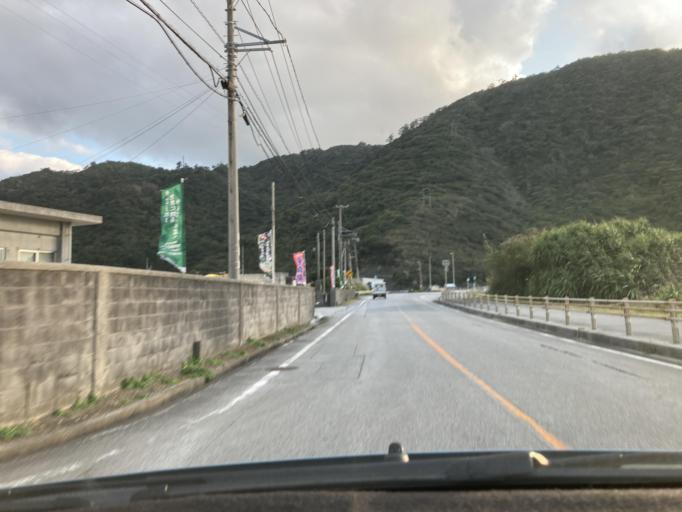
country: JP
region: Okinawa
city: Nago
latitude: 26.7990
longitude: 128.2326
